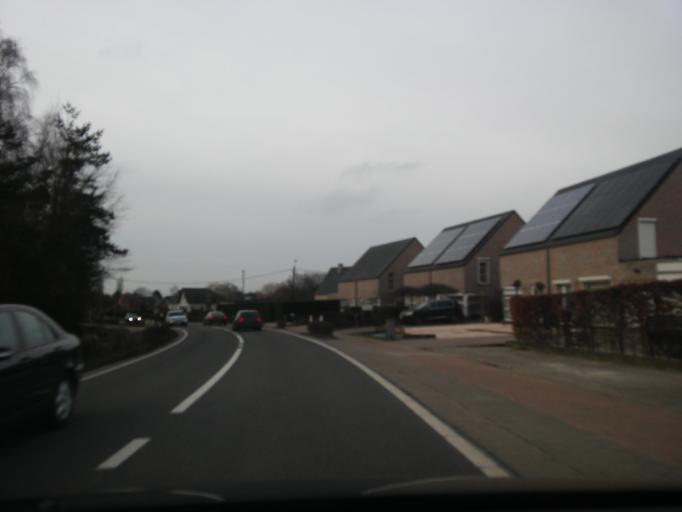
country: BE
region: Flanders
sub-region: Provincie Antwerpen
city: Herselt
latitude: 51.0516
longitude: 4.8899
